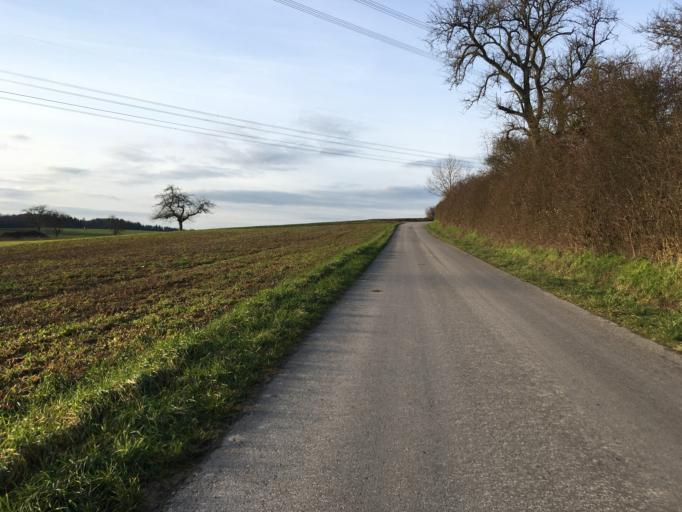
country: DE
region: Baden-Wuerttemberg
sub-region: Regierungsbezirk Stuttgart
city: Bad Wimpfen
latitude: 49.2237
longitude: 9.1339
